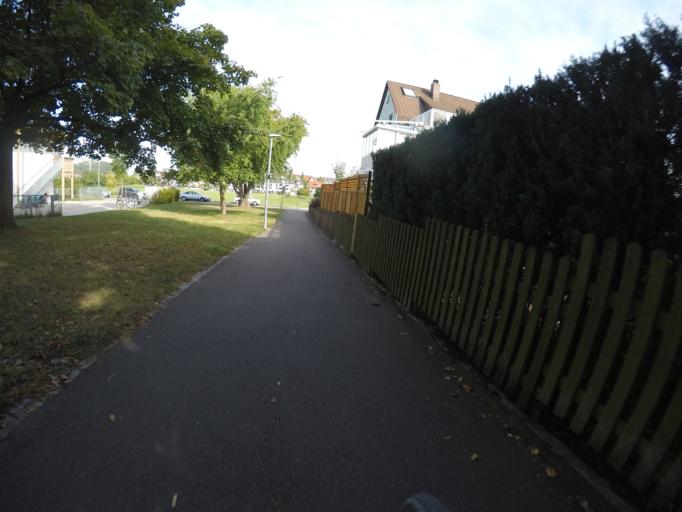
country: DE
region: Baden-Wuerttemberg
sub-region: Regierungsbezirk Stuttgart
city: Korntal
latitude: 48.8198
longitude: 9.1160
